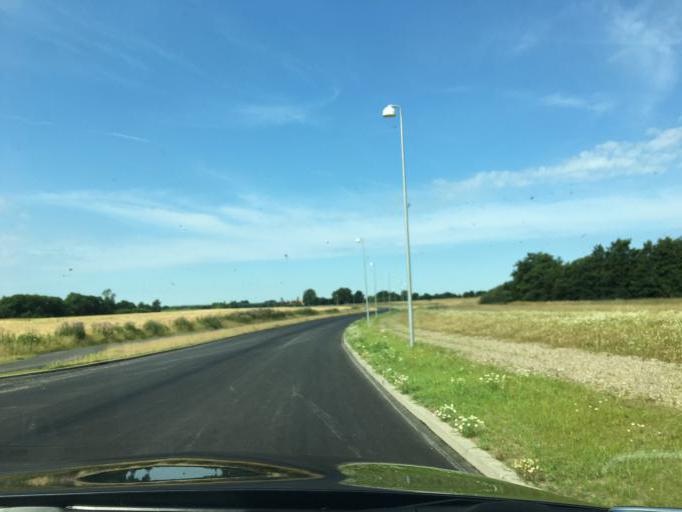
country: DK
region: South Denmark
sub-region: Kolding Kommune
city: Kolding
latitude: 55.5446
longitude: 9.4552
